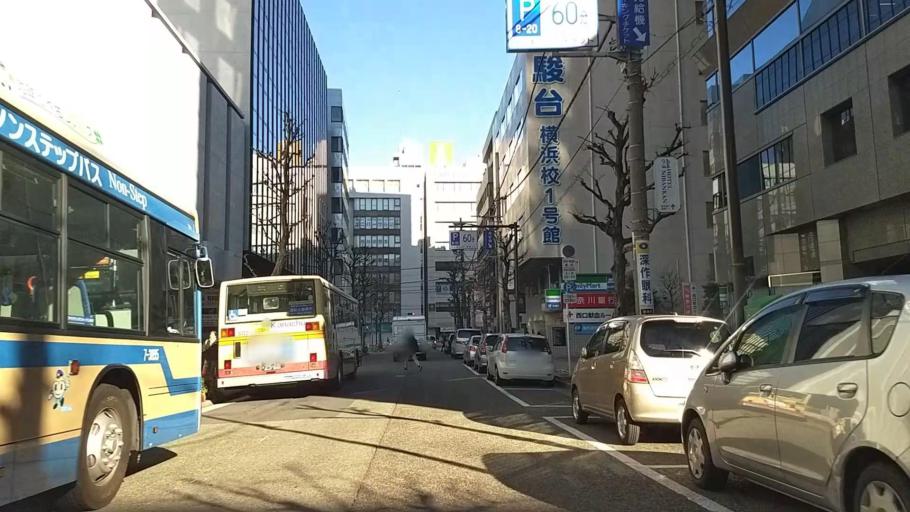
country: JP
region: Kanagawa
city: Yokohama
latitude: 35.4683
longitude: 139.6211
